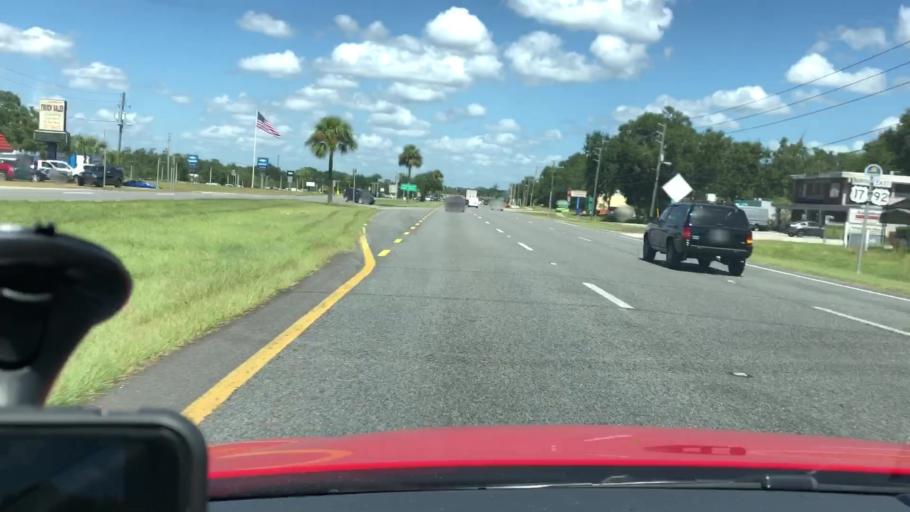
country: US
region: Florida
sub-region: Volusia County
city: Orange City
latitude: 28.9774
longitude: -81.2992
